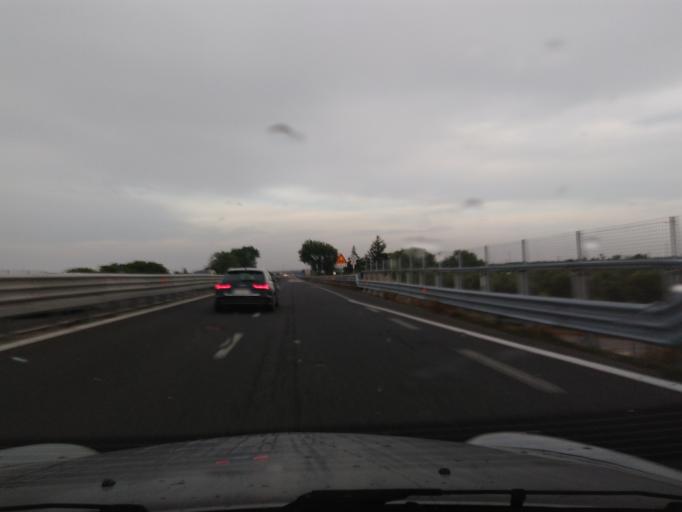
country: IT
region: Apulia
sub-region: Provincia di Bari
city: Giovinazzo
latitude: 41.1804
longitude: 16.6466
